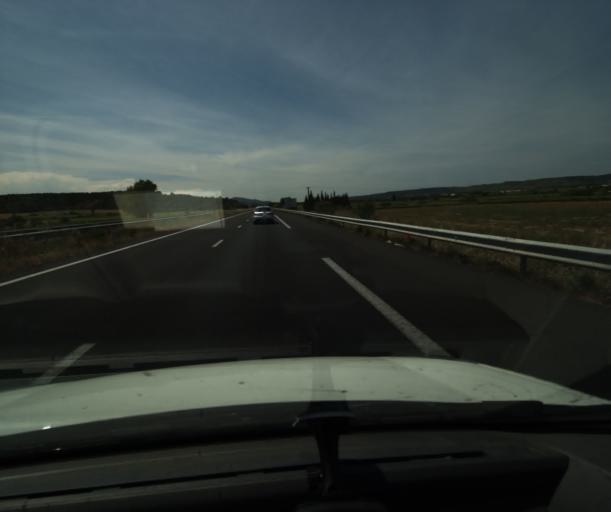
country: FR
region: Languedoc-Roussillon
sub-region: Departement de l'Aude
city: Lezignan-Corbieres
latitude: 43.1704
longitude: 2.7726
